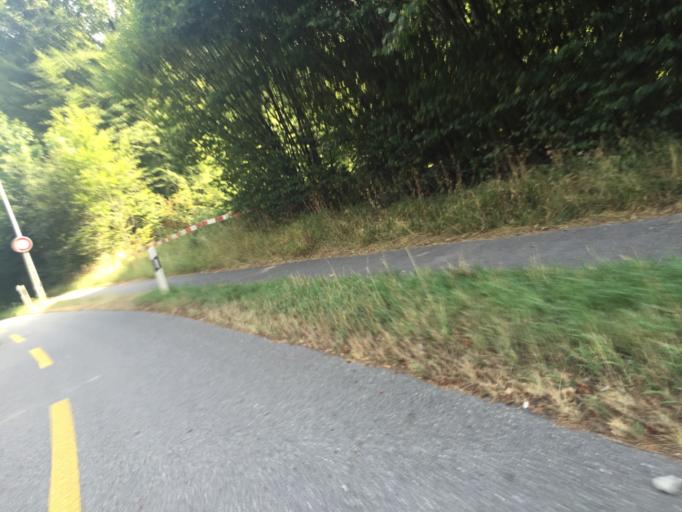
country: CH
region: Bern
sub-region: Bern-Mittelland District
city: Koniz
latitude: 46.9403
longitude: 7.4091
